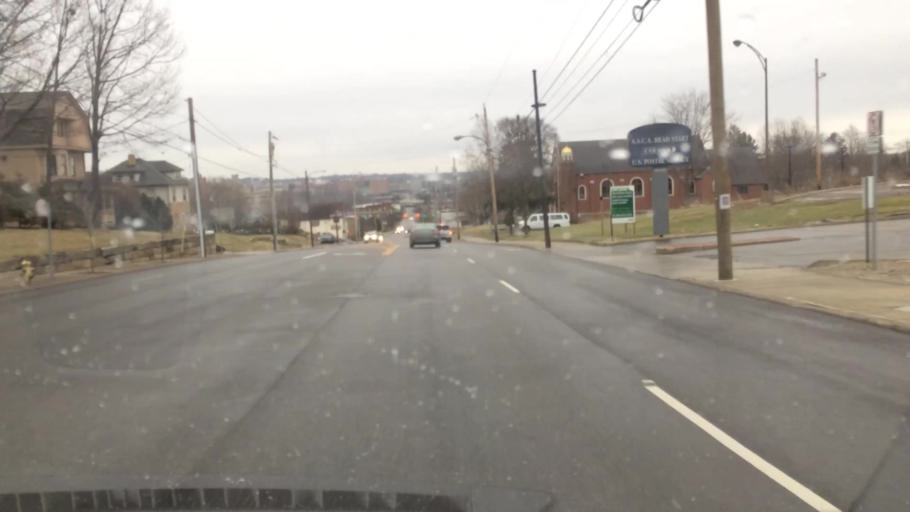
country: US
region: Ohio
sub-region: Summit County
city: Akron
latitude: 41.0880
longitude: -81.5402
